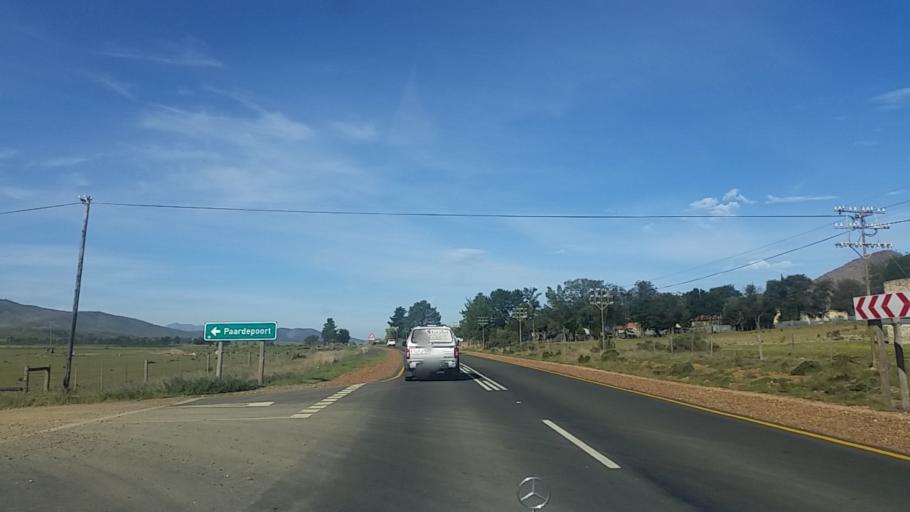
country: ZA
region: Western Cape
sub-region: Eden District Municipality
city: George
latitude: -33.8340
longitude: 22.4498
